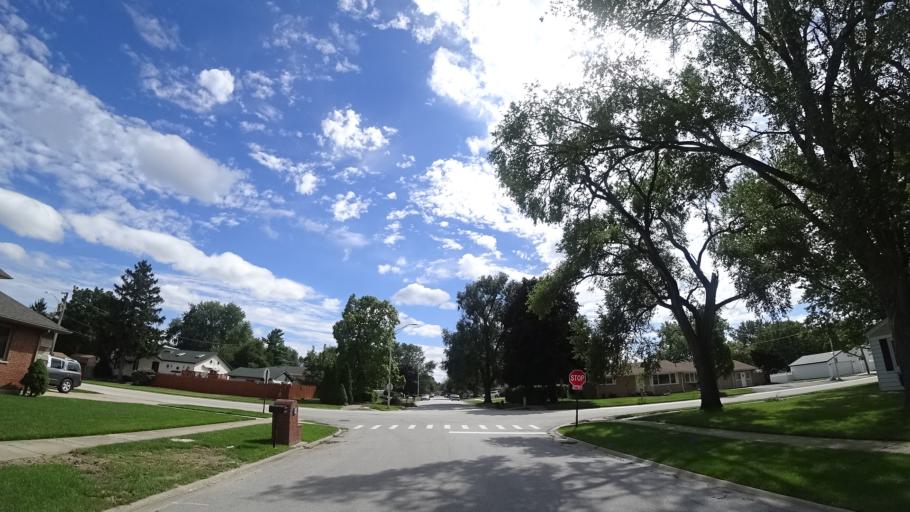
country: US
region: Illinois
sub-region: Cook County
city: Chicago Ridge
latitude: 41.7162
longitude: -87.7761
